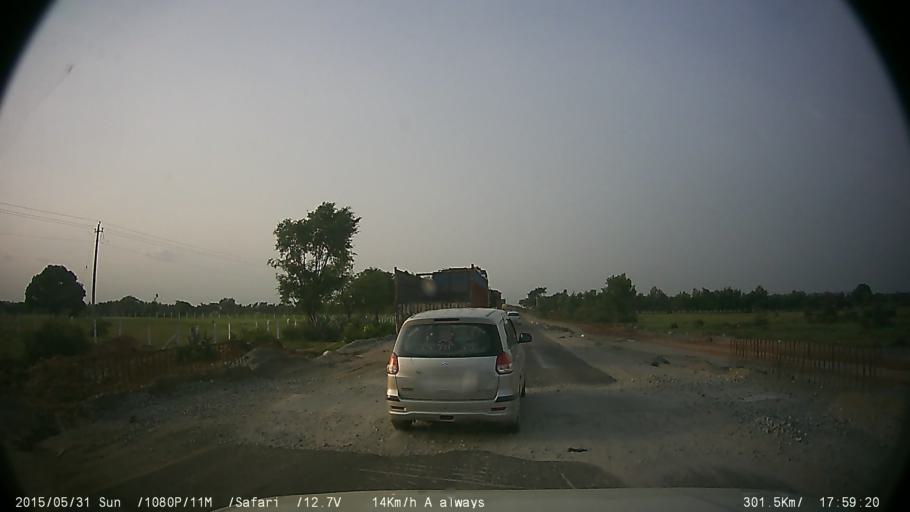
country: IN
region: Karnataka
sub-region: Mysore
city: Nanjangud
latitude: 12.0150
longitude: 76.6712
